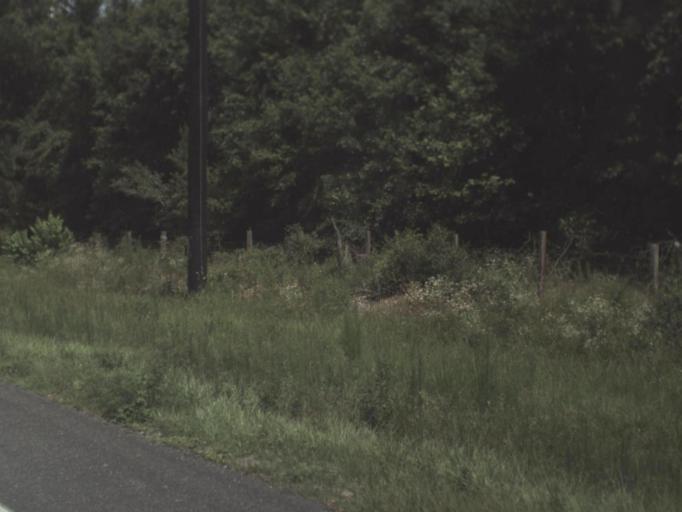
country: US
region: Florida
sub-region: Gilchrist County
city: Trenton
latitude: 29.6171
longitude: -82.7856
